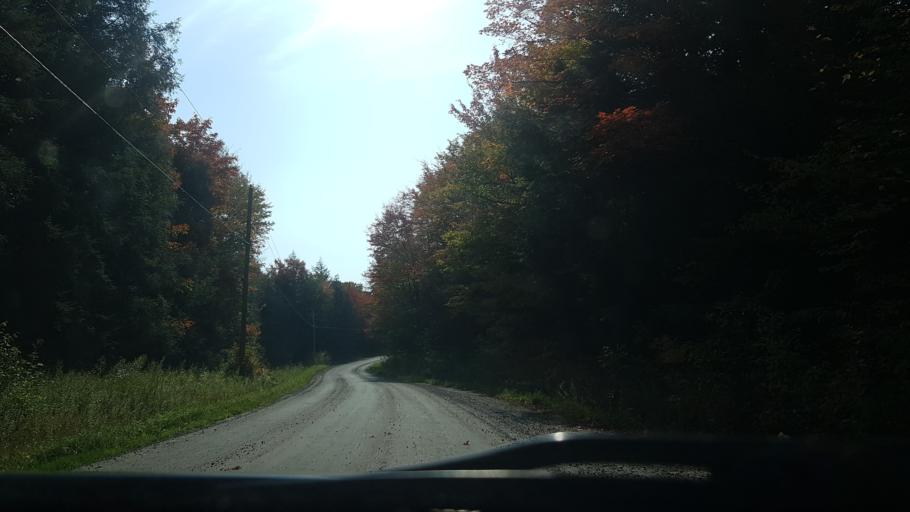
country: CA
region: Ontario
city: Bracebridge
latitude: 44.9325
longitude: -79.2368
